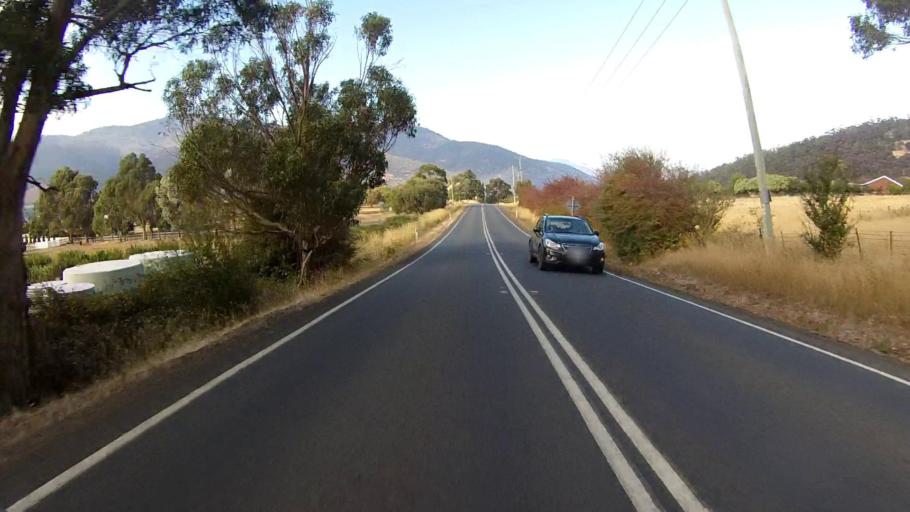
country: AU
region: Tasmania
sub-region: Brighton
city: Bridgewater
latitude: -42.7324
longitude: 147.1768
